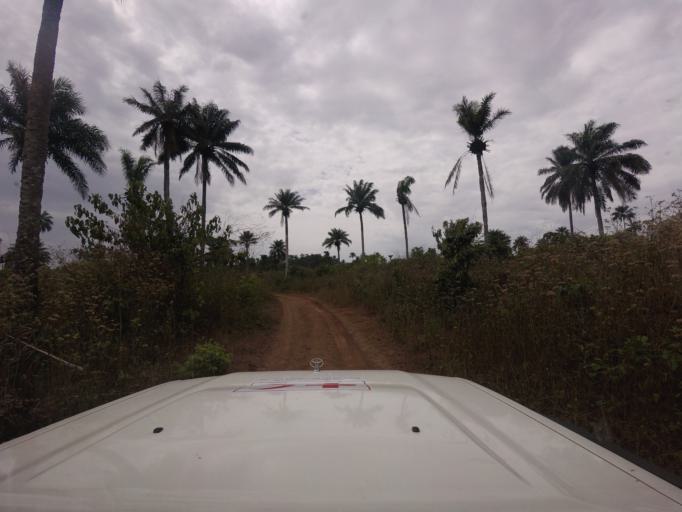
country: SL
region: Eastern Province
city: Buedu
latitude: 8.2373
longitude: -10.2627
